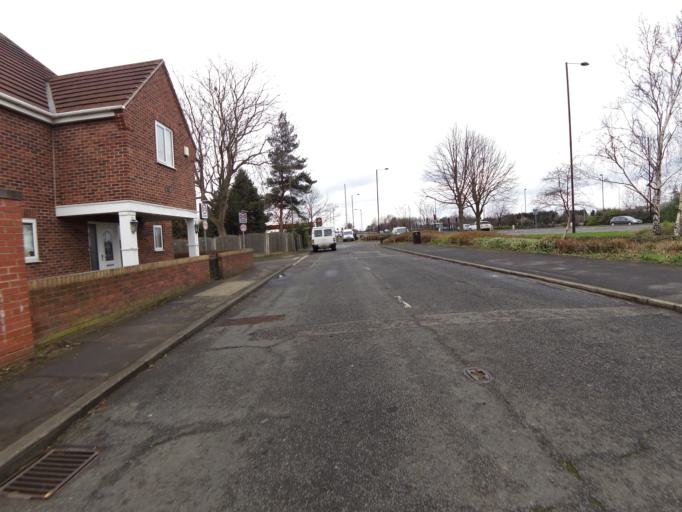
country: GB
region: England
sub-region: Doncaster
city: Bentley
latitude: 53.5309
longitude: -1.1502
